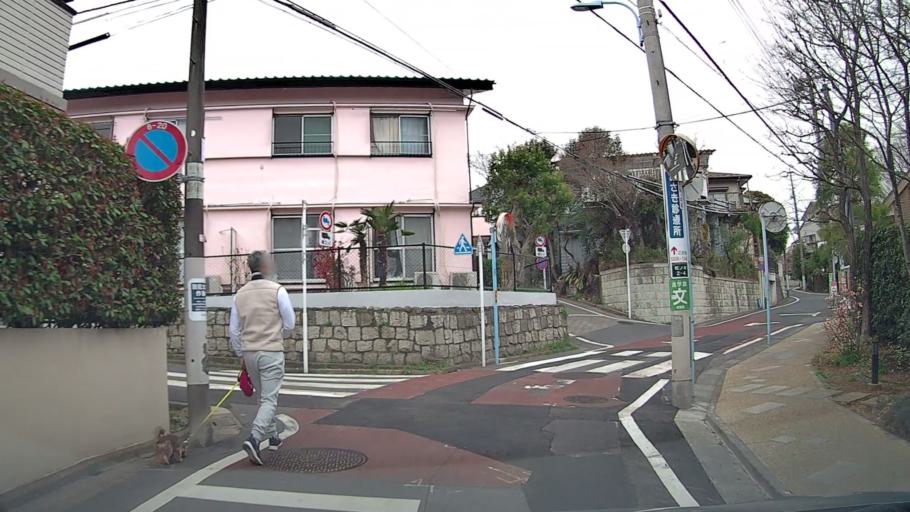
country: JP
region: Tokyo
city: Tokyo
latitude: 35.6899
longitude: 139.6439
